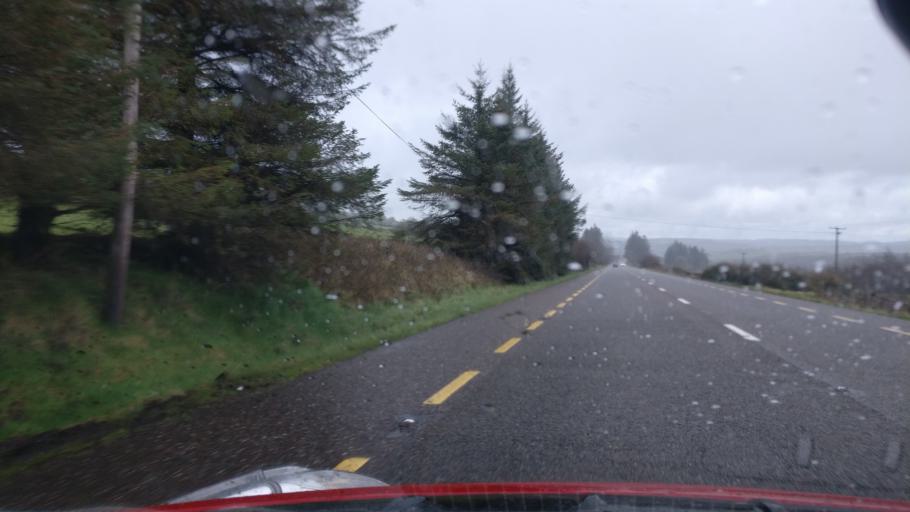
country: IE
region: Munster
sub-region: Ciarrai
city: Castleisland
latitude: 52.2893
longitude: -9.4016
